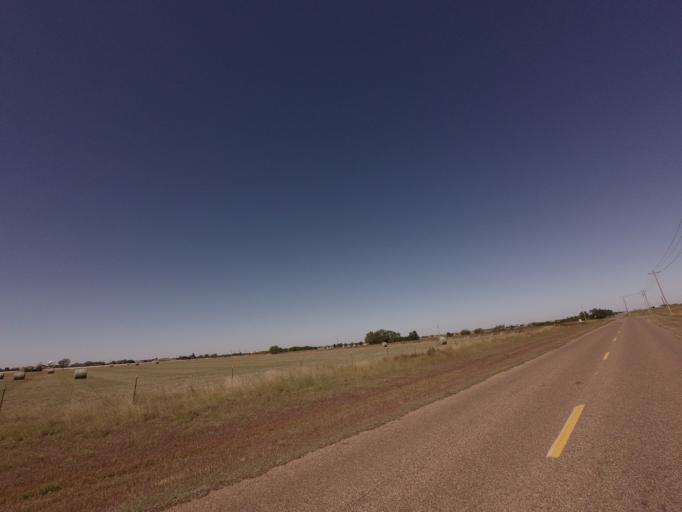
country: US
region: New Mexico
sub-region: Curry County
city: Clovis
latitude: 34.4320
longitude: -103.1608
